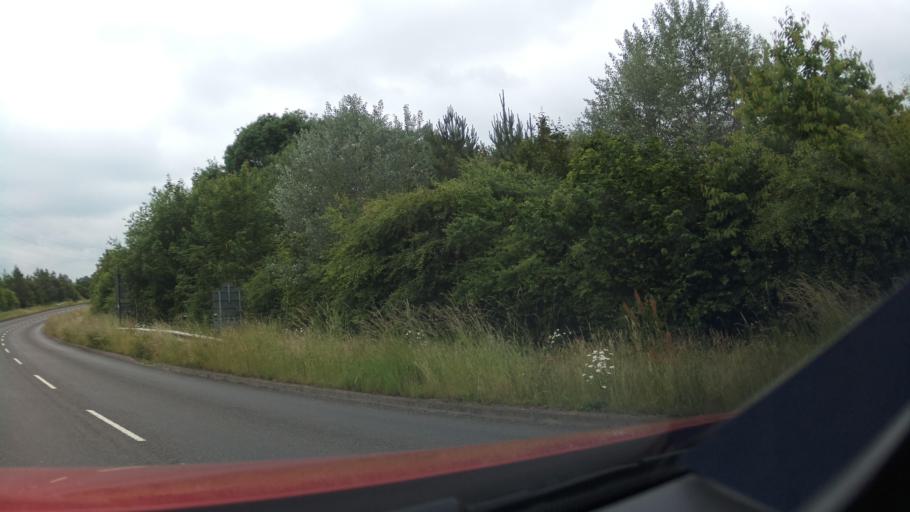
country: GB
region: England
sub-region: District of Rutland
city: Oakham
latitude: 52.6664
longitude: -0.7131
